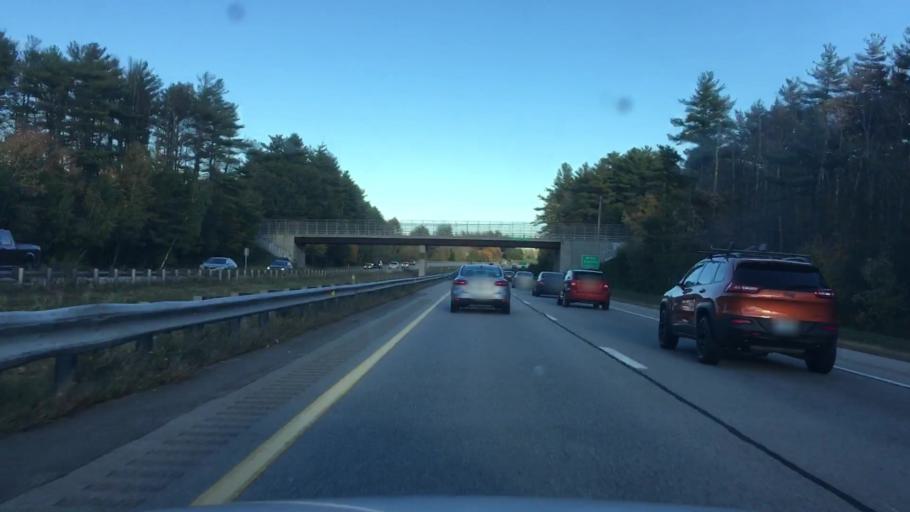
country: US
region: New Hampshire
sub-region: Rockingham County
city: Epping
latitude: 43.0268
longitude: -71.0878
